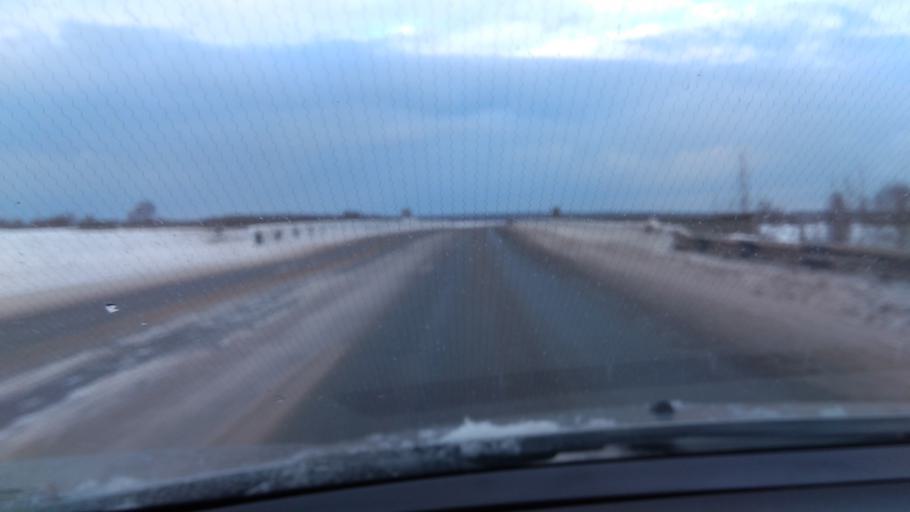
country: RU
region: Sverdlovsk
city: Nev'yansk
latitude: 57.5044
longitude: 60.1737
